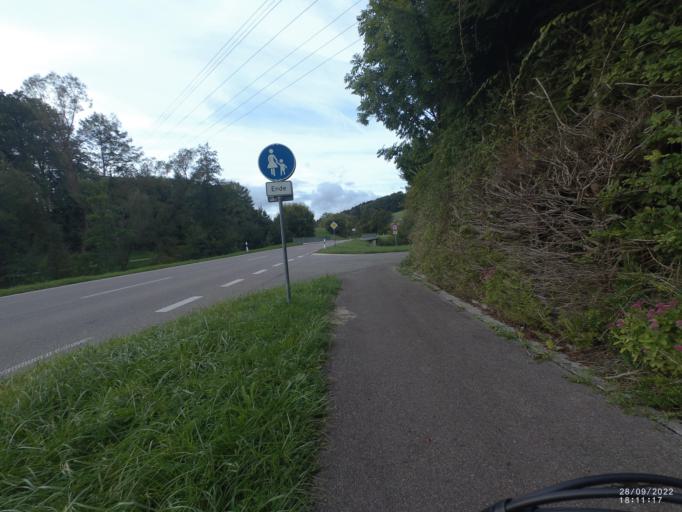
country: DE
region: Baden-Wuerttemberg
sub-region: Regierungsbezirk Stuttgart
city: Birenbach
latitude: 48.7463
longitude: 9.6484
